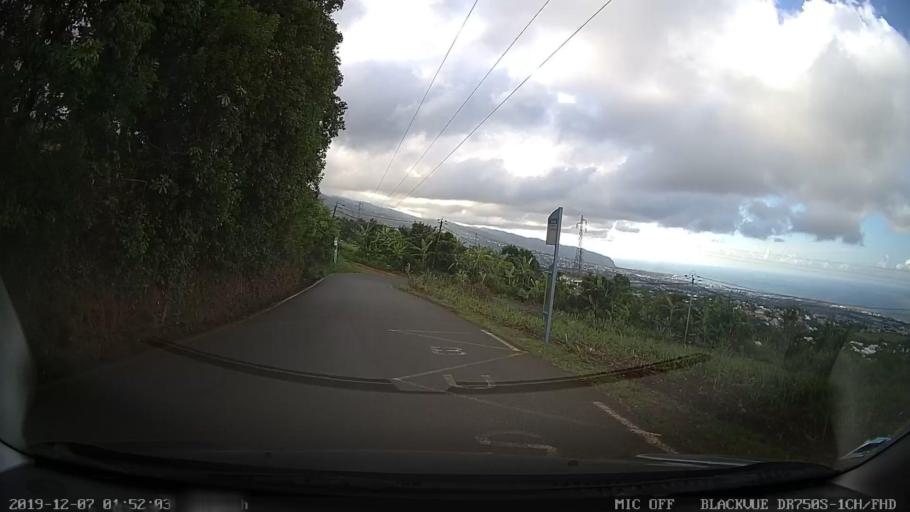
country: RE
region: Reunion
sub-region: Reunion
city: Sainte-Marie
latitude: -20.9407
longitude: 55.5344
